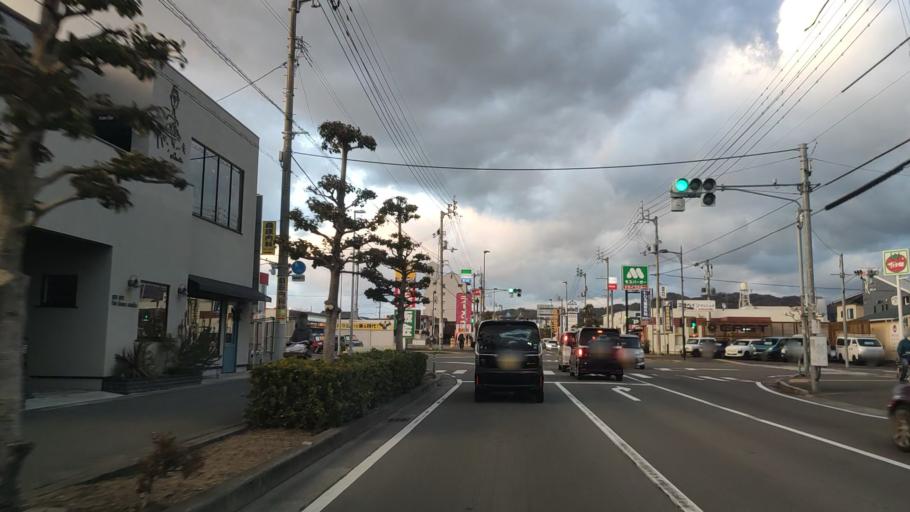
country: JP
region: Ehime
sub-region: Shikoku-chuo Shi
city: Matsuyama
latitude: 33.8326
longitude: 132.7873
